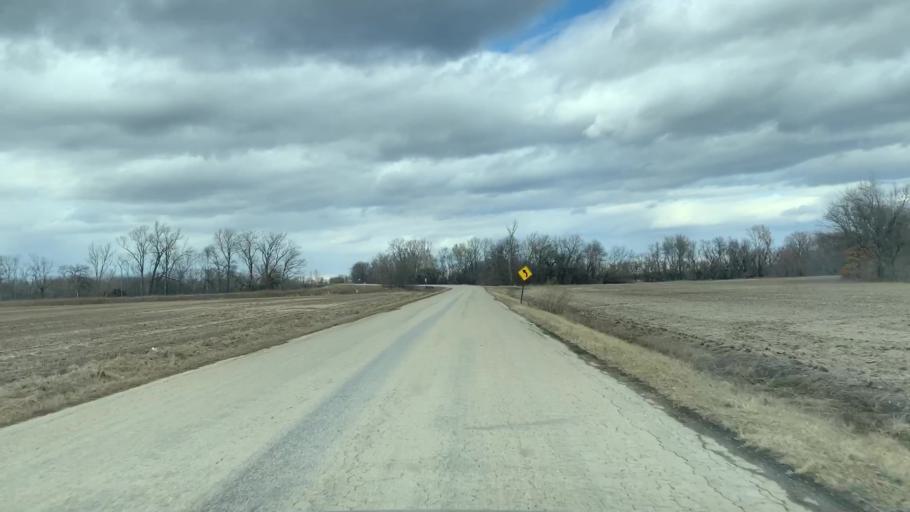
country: US
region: Kansas
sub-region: Allen County
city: Humboldt
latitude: 37.8002
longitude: -95.4705
